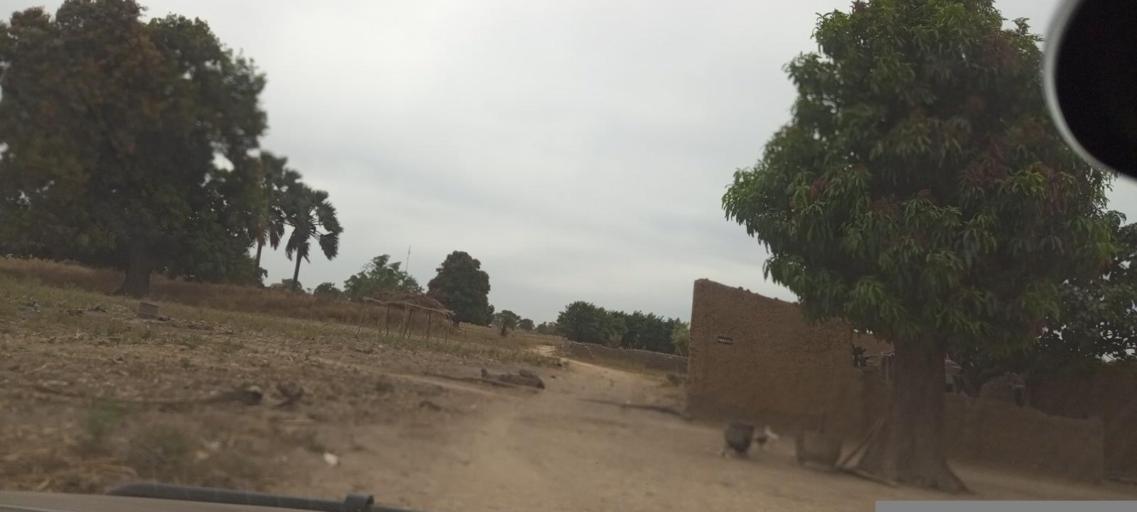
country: ML
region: Koulikoro
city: Kati
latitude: 12.7546
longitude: -8.3125
